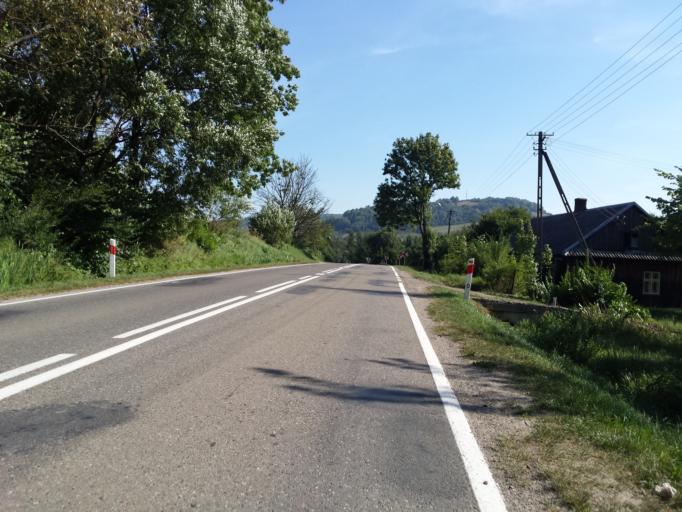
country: PL
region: Subcarpathian Voivodeship
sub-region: Powiat leski
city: Baligrod
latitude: 49.3264
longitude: 22.2831
